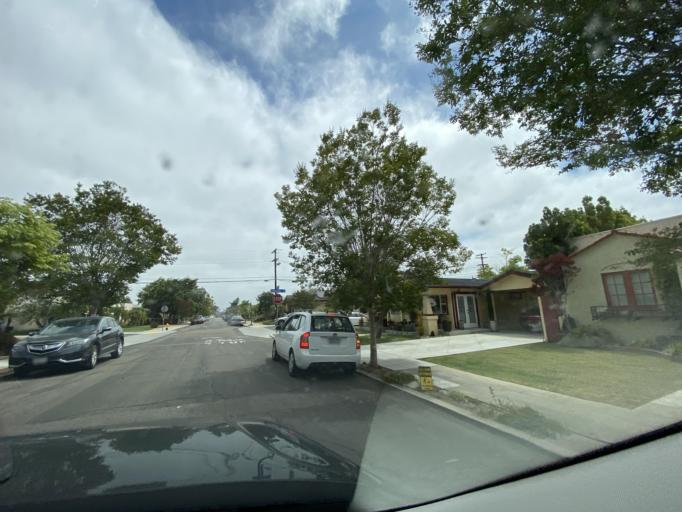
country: US
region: California
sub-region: San Diego County
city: San Diego
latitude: 32.7378
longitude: -117.1231
